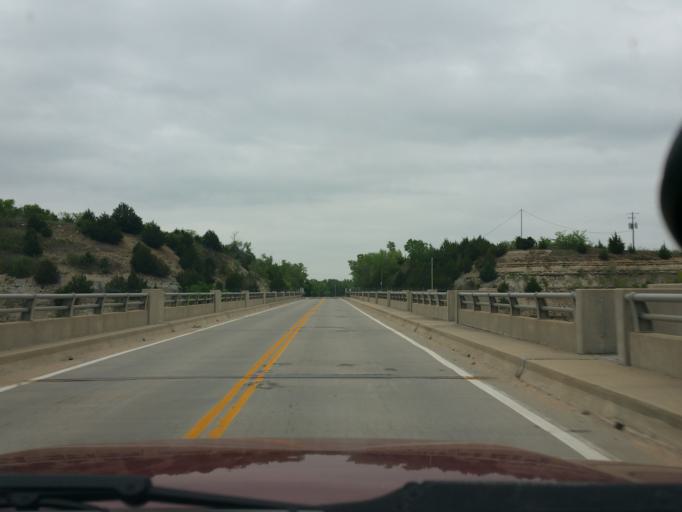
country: US
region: Kansas
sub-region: Riley County
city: Manhattan
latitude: 39.2637
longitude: -96.5781
